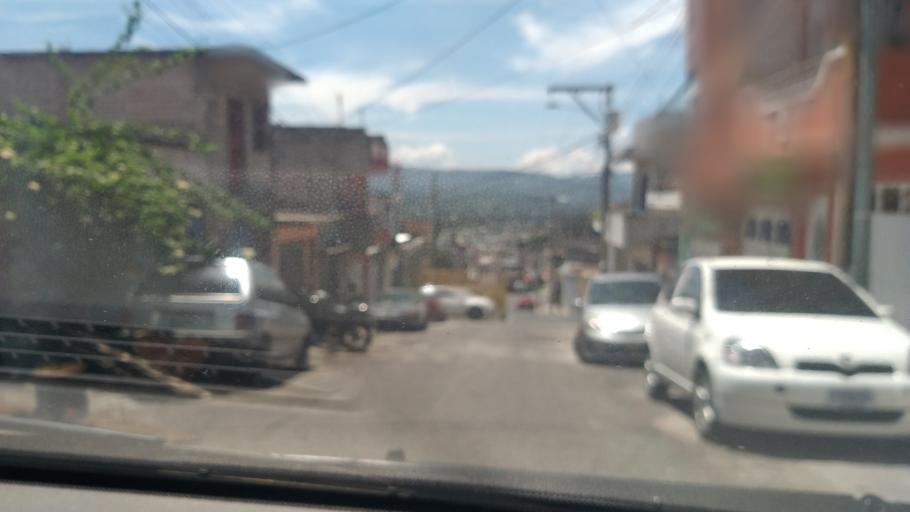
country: GT
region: Guatemala
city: Petapa
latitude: 14.5380
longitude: -90.5504
